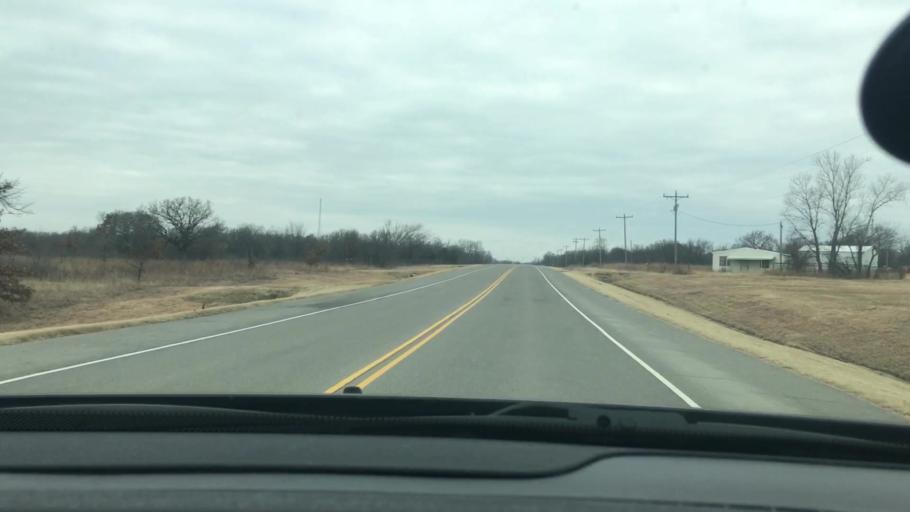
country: US
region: Oklahoma
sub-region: Carter County
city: Healdton
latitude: 34.4807
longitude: -97.4629
